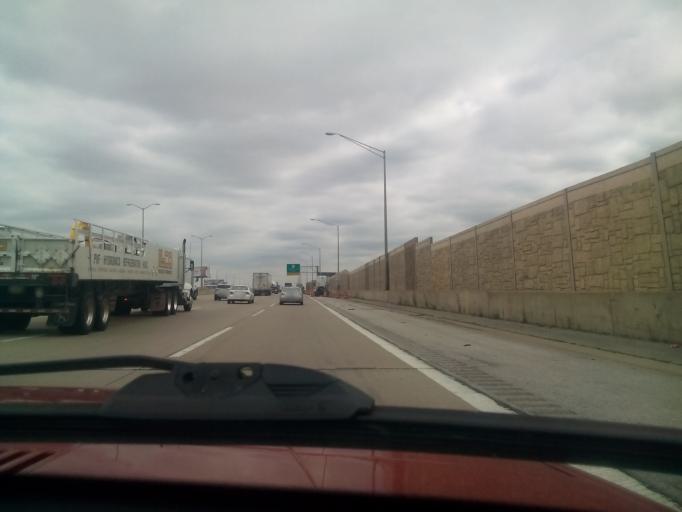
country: US
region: Illinois
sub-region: Cook County
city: East Hazel Crest
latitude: 41.5779
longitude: -87.6648
